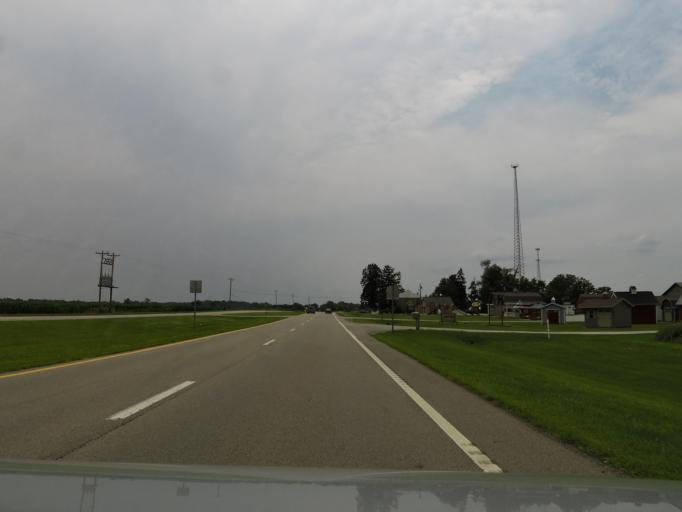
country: US
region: Ohio
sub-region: Greene County
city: Bellbrook
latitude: 39.6209
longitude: -83.9906
